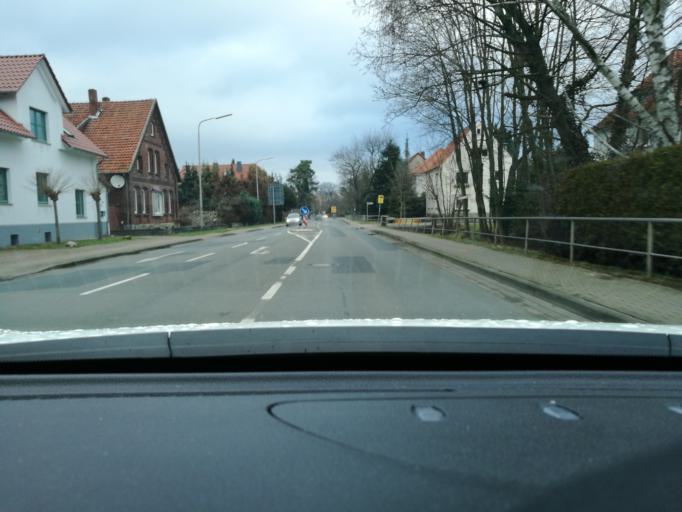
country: DE
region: Lower Saxony
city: Stadthagen
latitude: 52.3167
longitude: 9.2029
